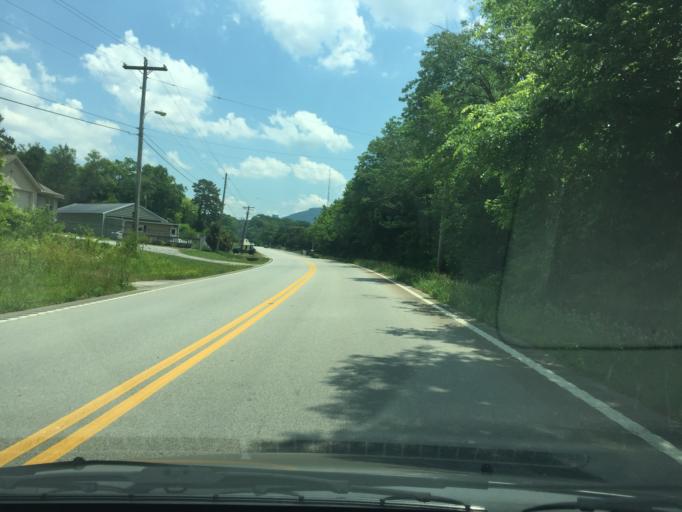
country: US
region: Tennessee
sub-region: Hamilton County
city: Lookout Mountain
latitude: 35.0252
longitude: -85.4019
